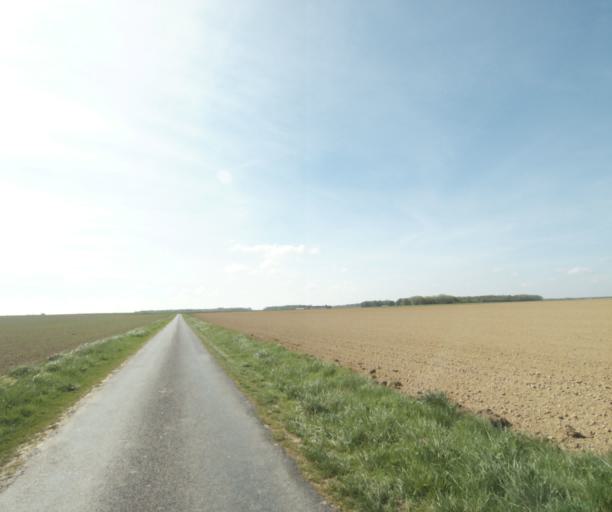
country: FR
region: Ile-de-France
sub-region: Departement de Seine-et-Marne
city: Nangis
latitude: 48.5392
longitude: 3.0374
